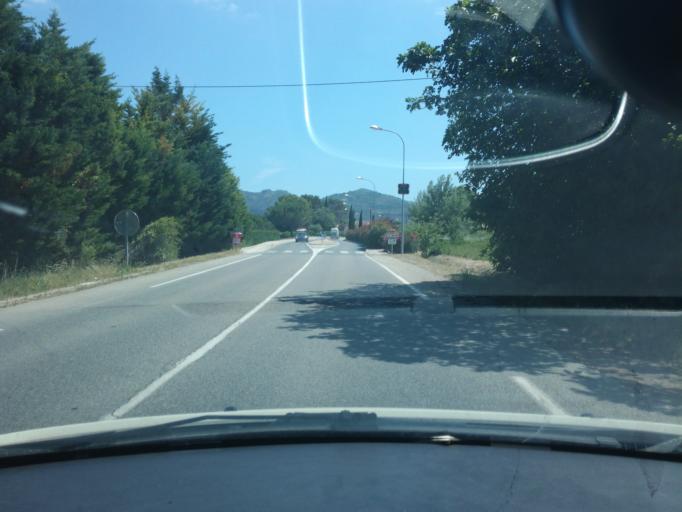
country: FR
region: Provence-Alpes-Cote d'Azur
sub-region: Departement du Var
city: Le Muy
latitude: 43.4798
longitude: 6.5655
